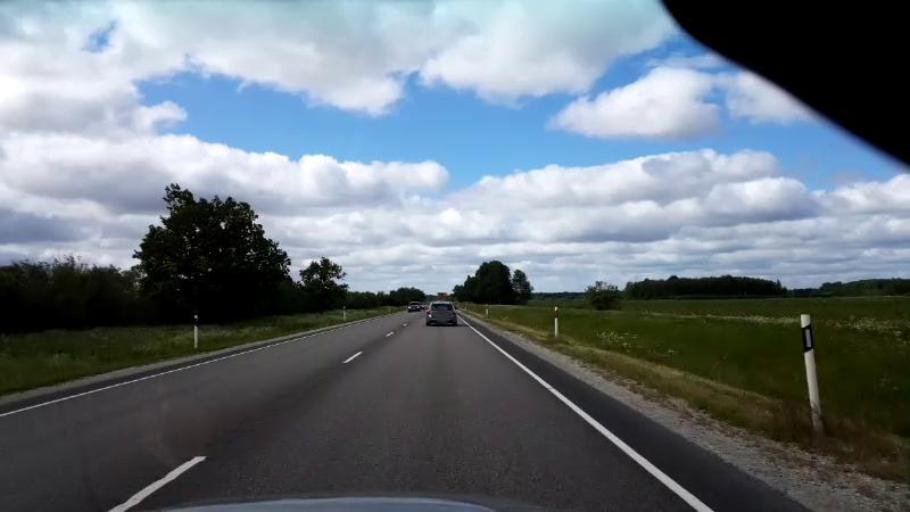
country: EE
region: Paernumaa
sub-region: Sauga vald
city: Sauga
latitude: 58.5024
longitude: 24.5410
